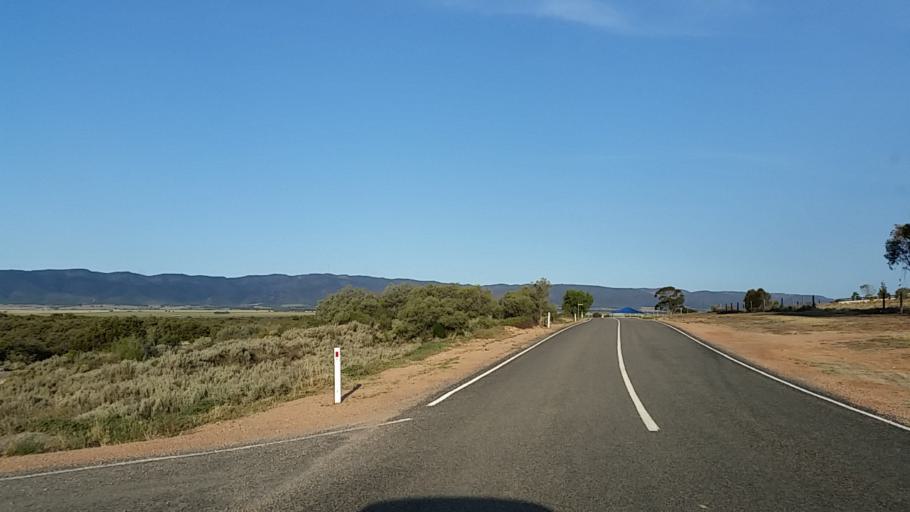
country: AU
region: South Australia
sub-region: Port Pirie City and Dists
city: Port Pirie
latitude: -33.0991
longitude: 138.0309
